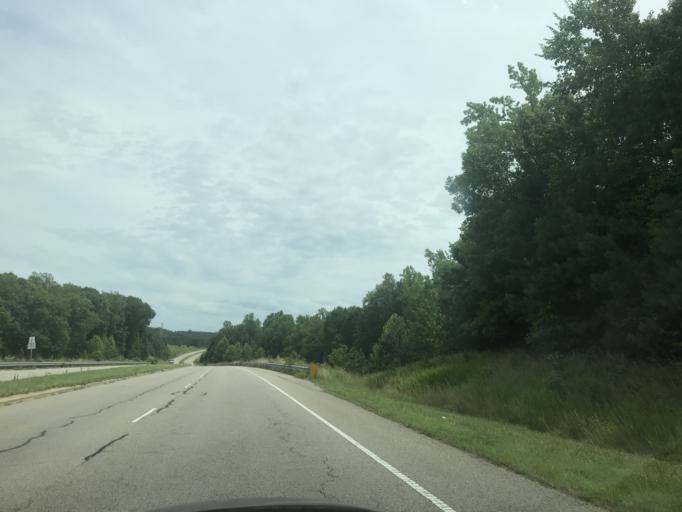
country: US
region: North Carolina
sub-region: Vance County
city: South Henderson
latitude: 36.3059
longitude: -78.4407
